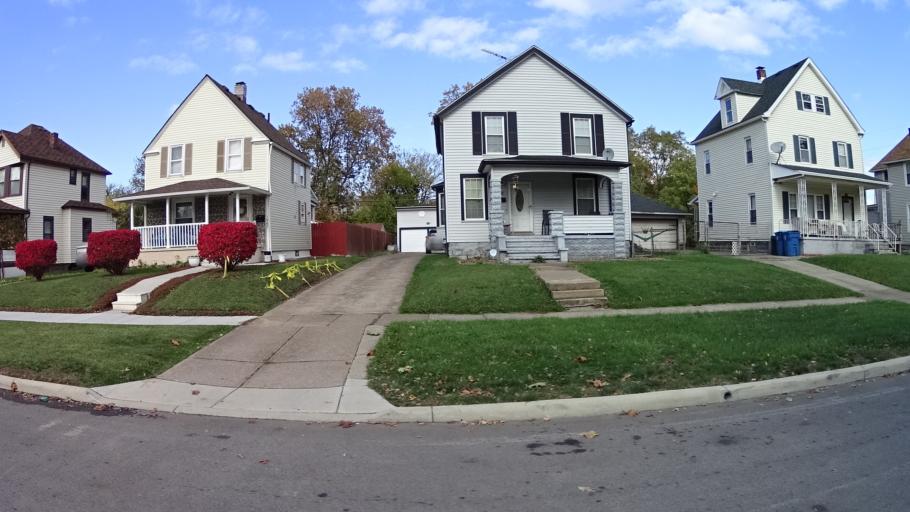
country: US
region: Ohio
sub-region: Lorain County
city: Sheffield
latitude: 41.4435
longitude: -82.1287
